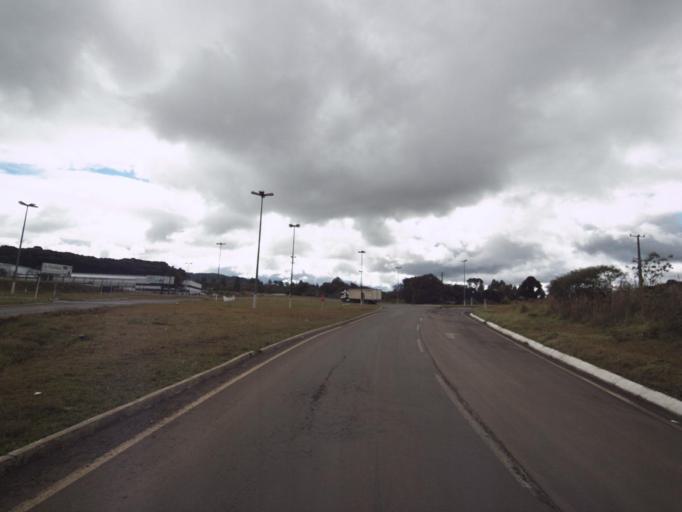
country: BR
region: Santa Catarina
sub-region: Concordia
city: Concordia
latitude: -27.2249
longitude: -51.9501
